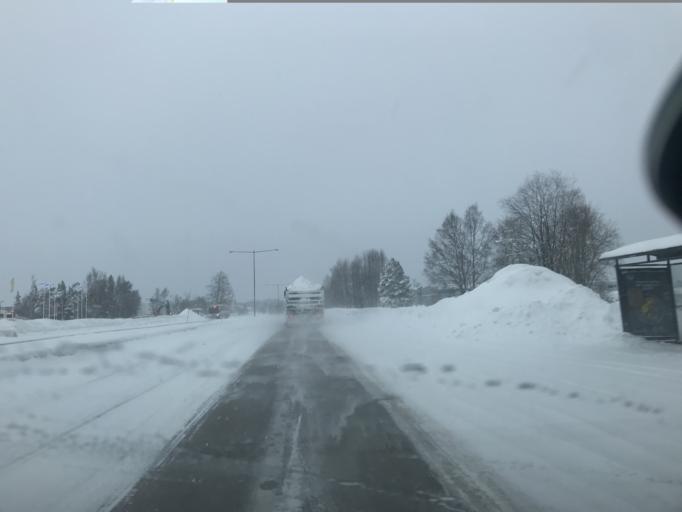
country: SE
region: Norrbotten
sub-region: Lulea Kommun
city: Lulea
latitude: 65.6089
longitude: 22.1373
